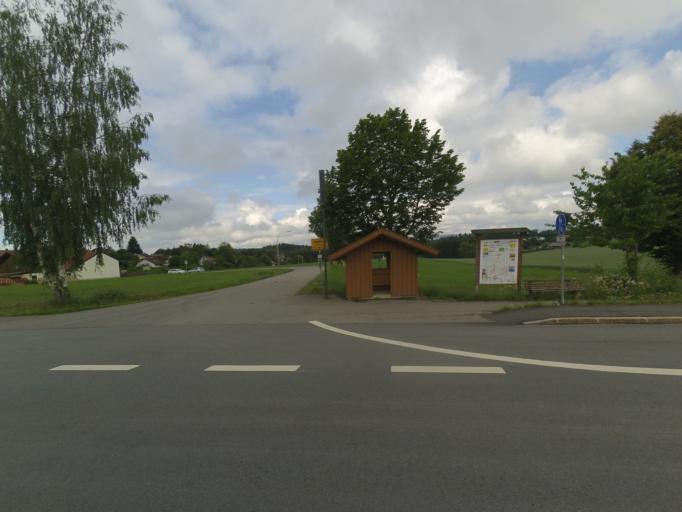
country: DE
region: Bavaria
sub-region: Lower Bavaria
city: Haselbach
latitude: 48.9900
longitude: 12.6901
